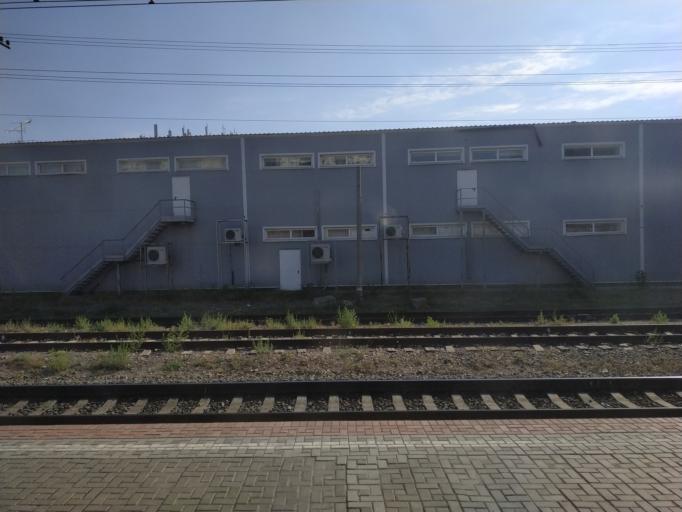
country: RU
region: Volgograd
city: Volgograd
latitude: 48.7271
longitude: 44.5293
